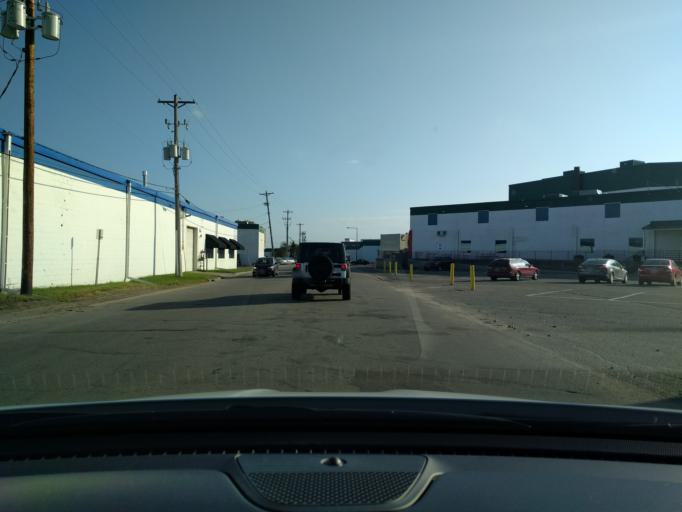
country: US
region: Minnesota
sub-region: Ramsey County
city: Falcon Heights
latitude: 44.9649
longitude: -93.1891
